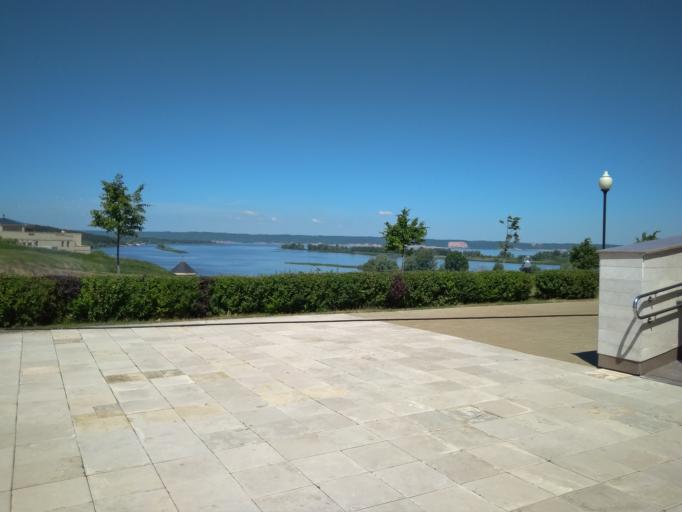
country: RU
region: Tatarstan
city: Bolgar
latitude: 54.9857
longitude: 49.0524
